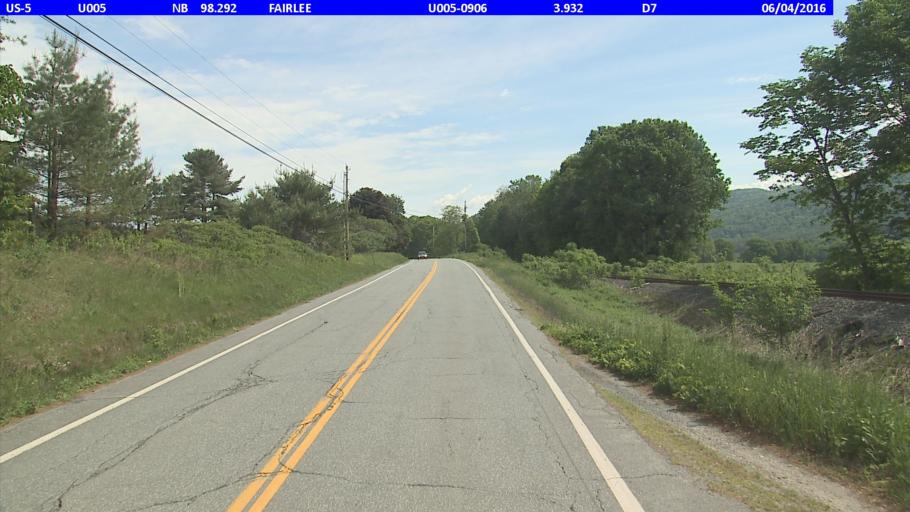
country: US
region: New Hampshire
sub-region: Grafton County
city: Orford
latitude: 43.9155
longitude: -72.1311
